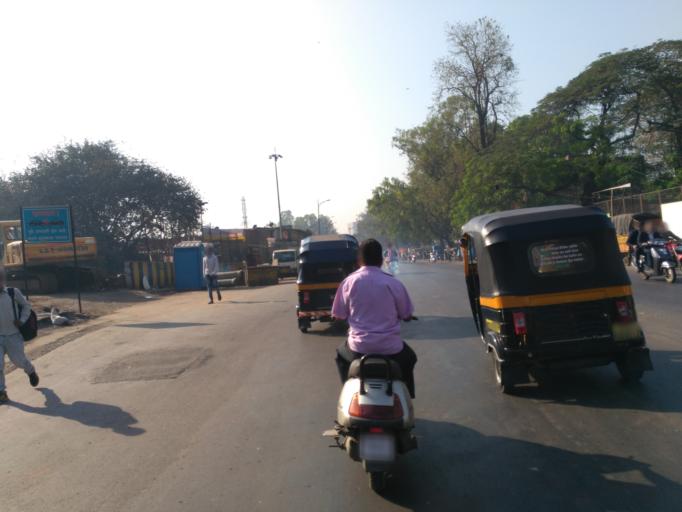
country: IN
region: Maharashtra
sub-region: Pune Division
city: Pune
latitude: 18.4986
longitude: 73.8694
